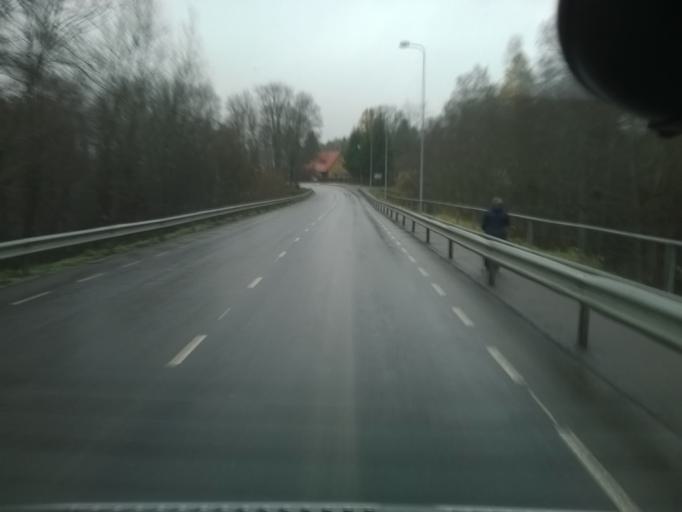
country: EE
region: Harju
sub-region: Saku vald
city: Saku
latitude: 59.2341
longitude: 24.6824
